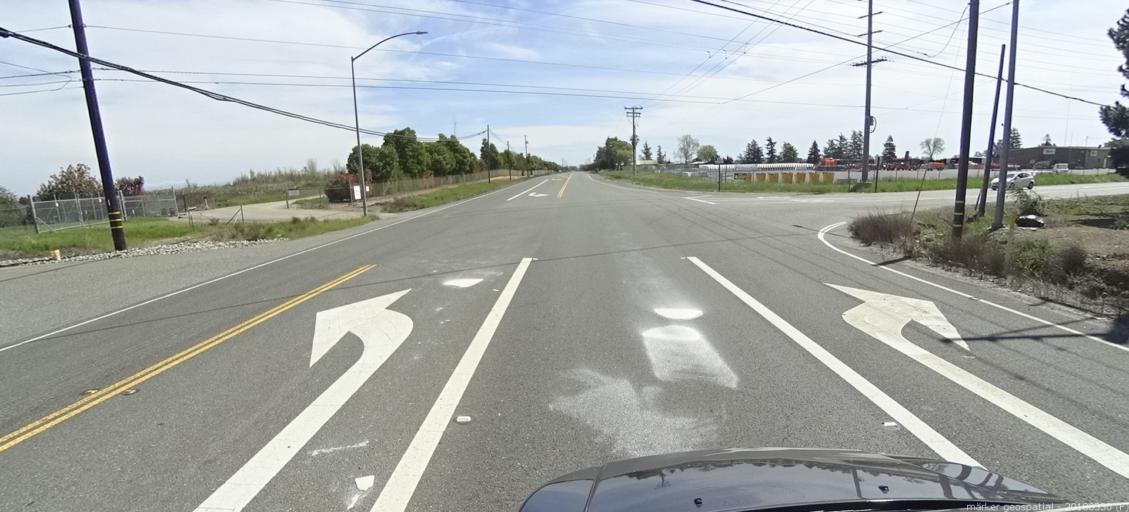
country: US
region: California
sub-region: Sacramento County
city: Rosemont
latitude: 38.5315
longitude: -121.3445
